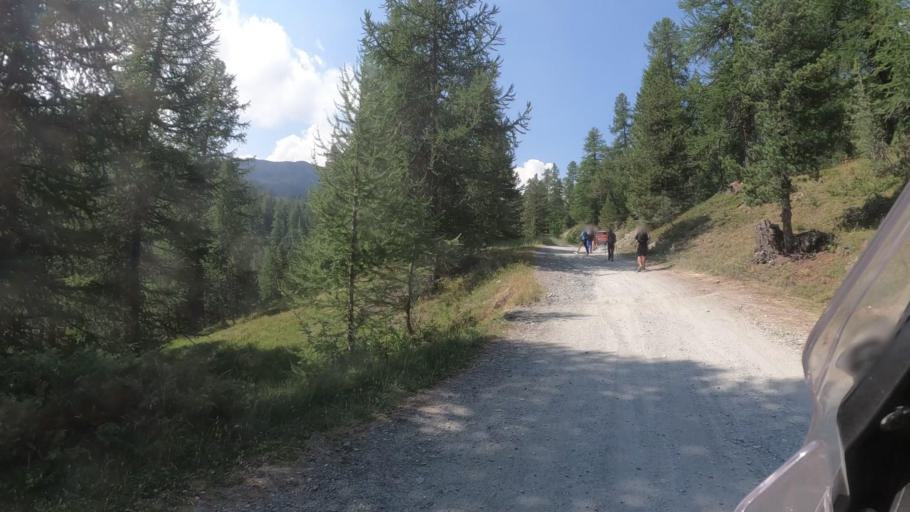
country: IT
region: Piedmont
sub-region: Provincia di Torino
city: Cesana Torinese
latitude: 44.9093
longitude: 6.7999
